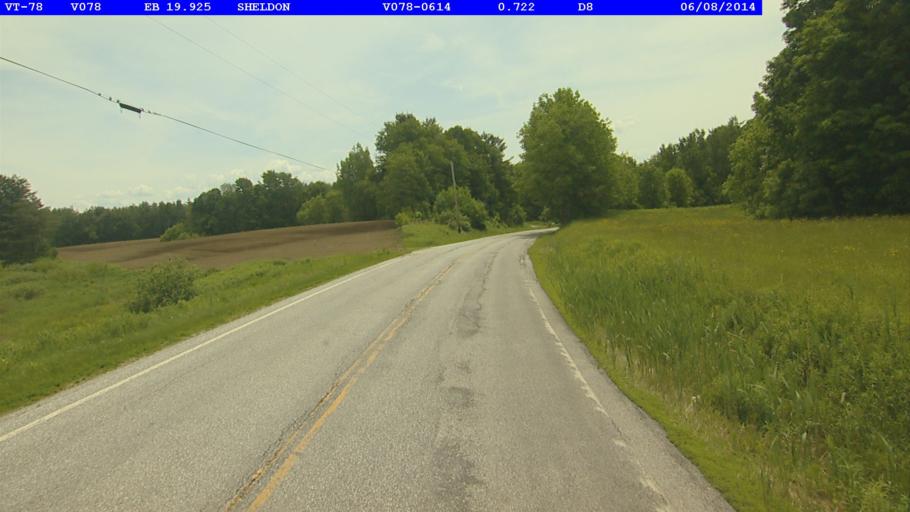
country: US
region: Vermont
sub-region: Franklin County
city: Enosburg Falls
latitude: 44.9161
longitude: -72.9596
